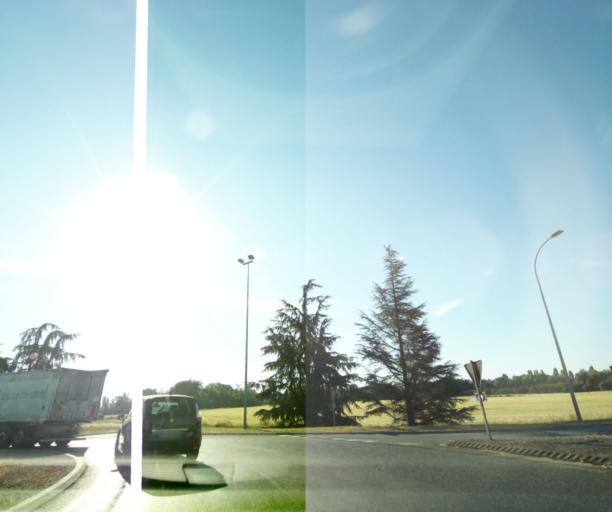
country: FR
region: Ile-de-France
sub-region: Departement de Seine-et-Marne
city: Montereau-Fault-Yonne
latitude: 48.3808
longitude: 2.9644
